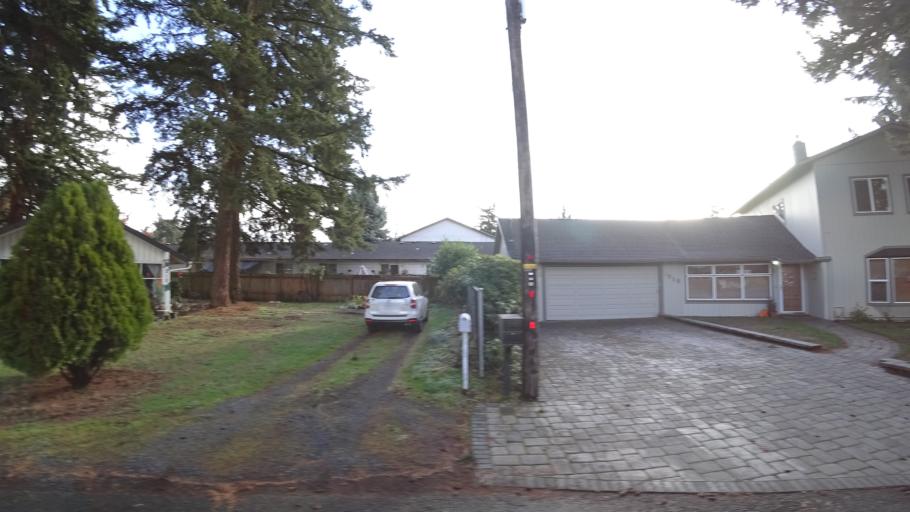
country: US
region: Oregon
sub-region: Multnomah County
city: Lents
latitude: 45.5243
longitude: -122.5424
